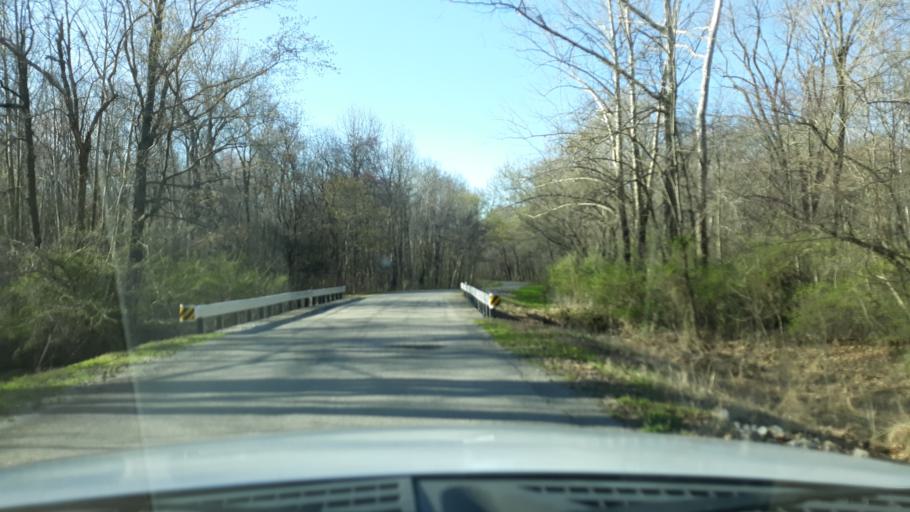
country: US
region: Illinois
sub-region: Saline County
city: Harrisburg
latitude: 37.7590
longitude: -88.5692
